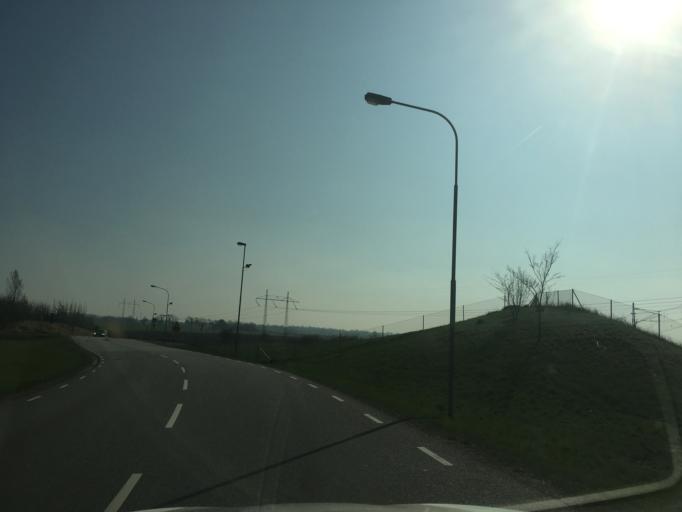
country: SE
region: Skane
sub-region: Staffanstorps Kommun
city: Hjaerup
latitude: 55.6700
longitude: 13.1302
